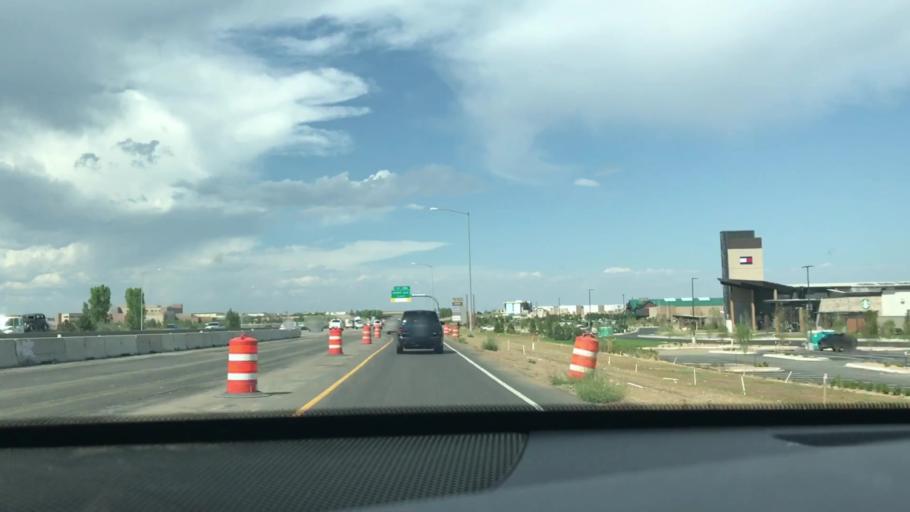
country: US
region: Colorado
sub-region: Adams County
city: Northglenn
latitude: 39.9474
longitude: -104.9865
